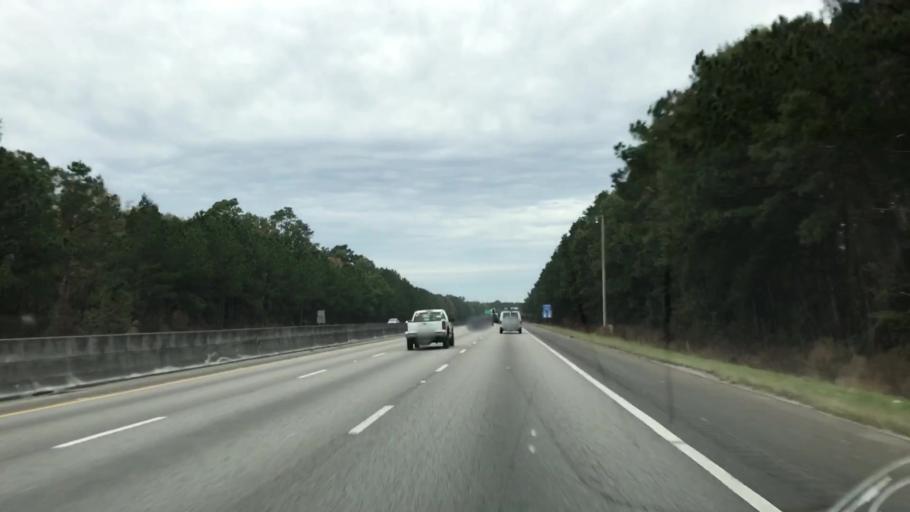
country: US
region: South Carolina
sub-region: Berkeley County
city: Goose Creek
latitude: 32.9548
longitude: -80.0649
